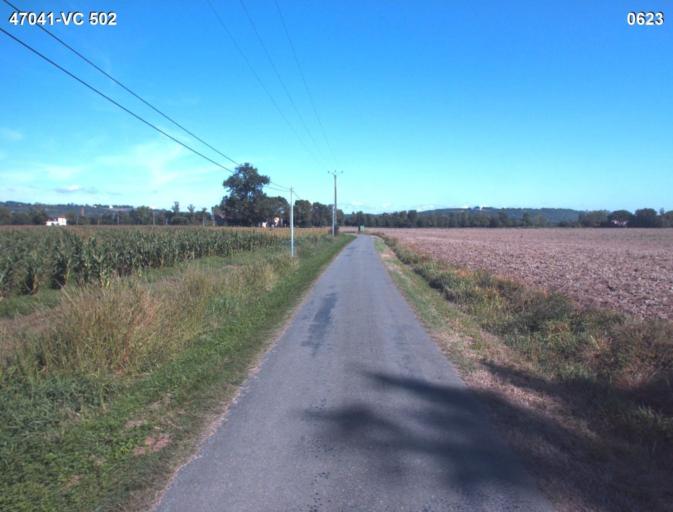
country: FR
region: Aquitaine
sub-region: Departement du Lot-et-Garonne
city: Port-Sainte-Marie
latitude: 44.2265
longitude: 0.3957
